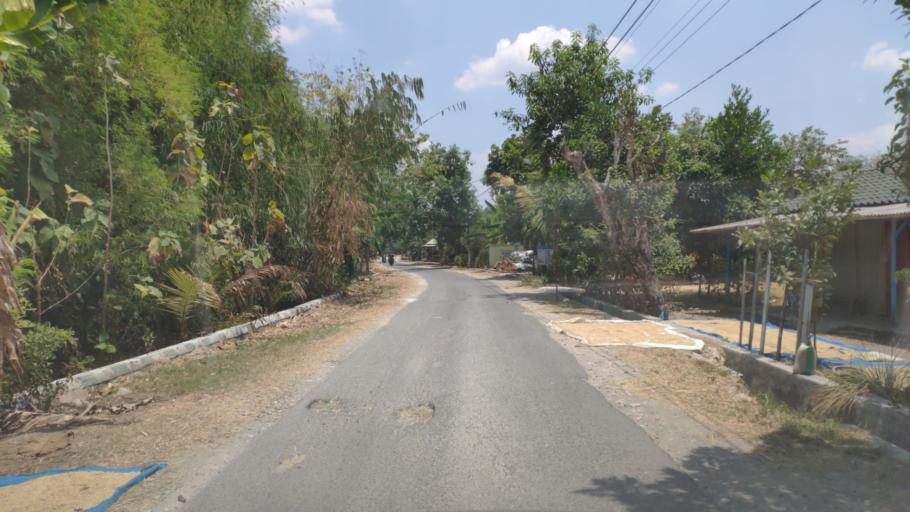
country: ID
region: East Java
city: Ketawang
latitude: -7.2056
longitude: 111.5478
